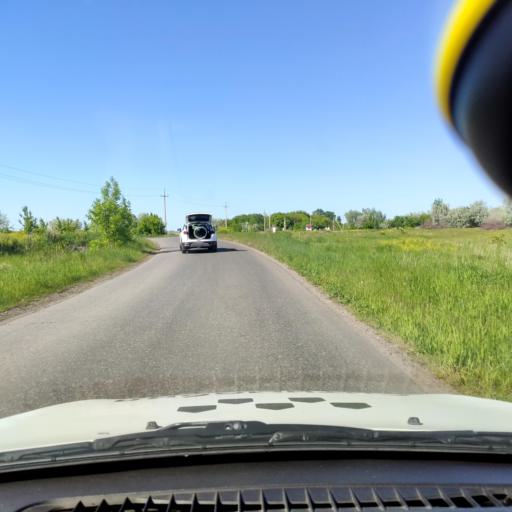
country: RU
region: Samara
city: Tol'yatti
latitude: 53.6569
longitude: 49.3315
